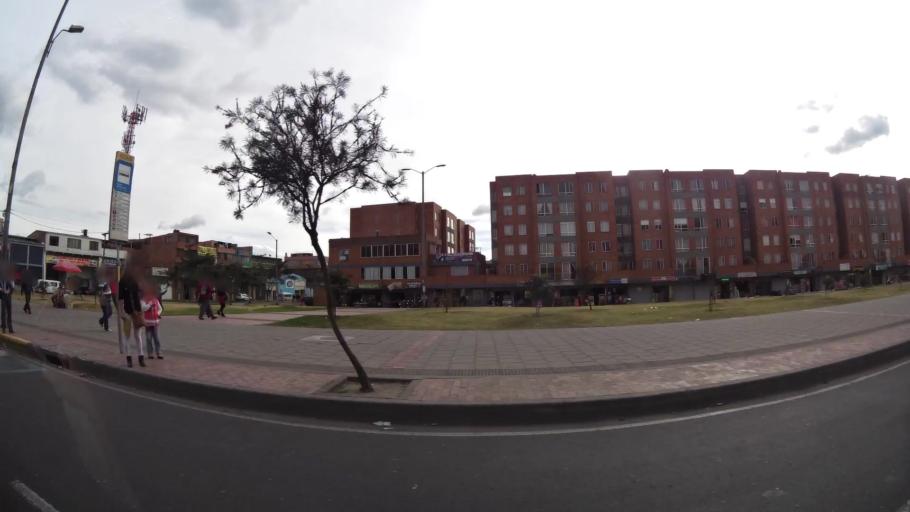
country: CO
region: Bogota D.C.
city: Bogota
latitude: 4.6385
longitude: -74.1554
